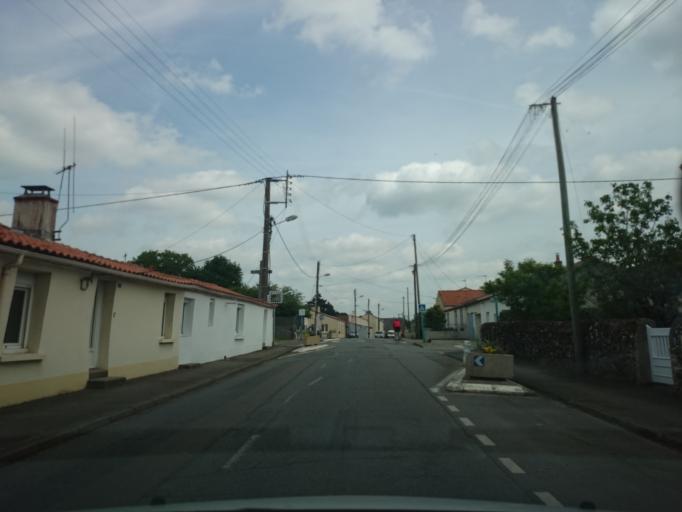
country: FR
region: Pays de la Loire
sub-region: Departement de la Loire-Atlantique
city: Pont-Saint-Martin
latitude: 47.1242
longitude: -1.5891
